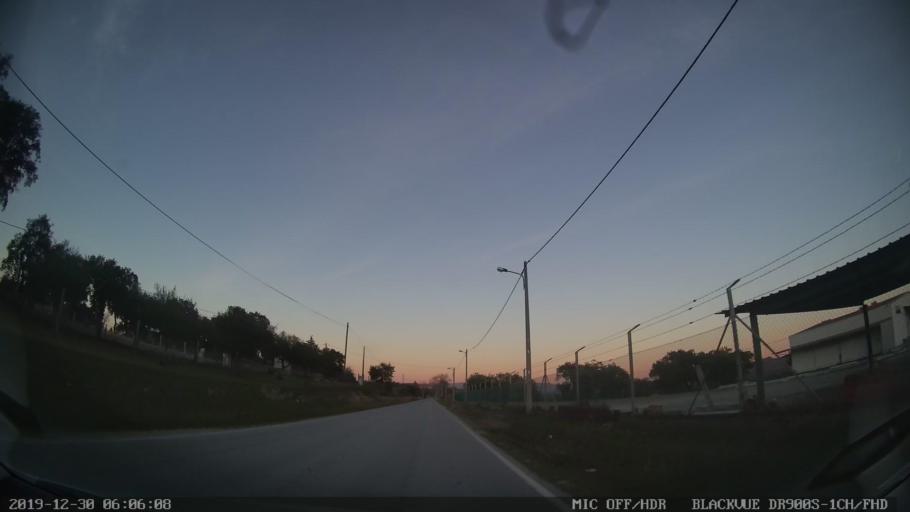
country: PT
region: Castelo Branco
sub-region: Penamacor
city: Penamacor
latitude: 40.0962
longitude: -7.2332
